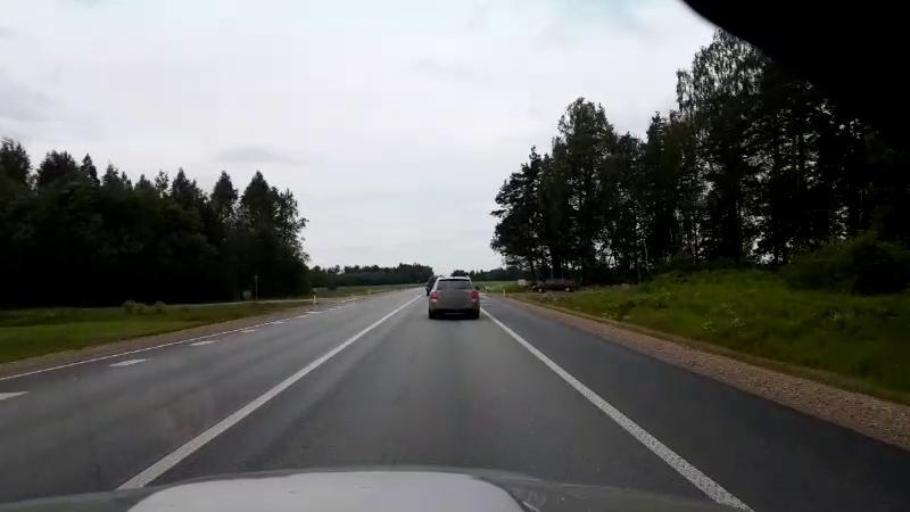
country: LV
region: Lecava
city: Iecava
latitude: 56.6511
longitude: 24.2294
